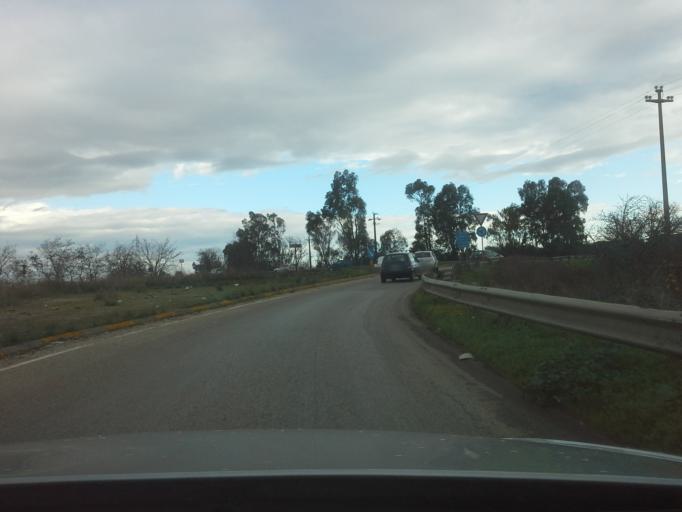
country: IT
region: Apulia
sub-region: Provincia di Bari
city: Cellamare
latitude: 41.0025
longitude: 16.9109
